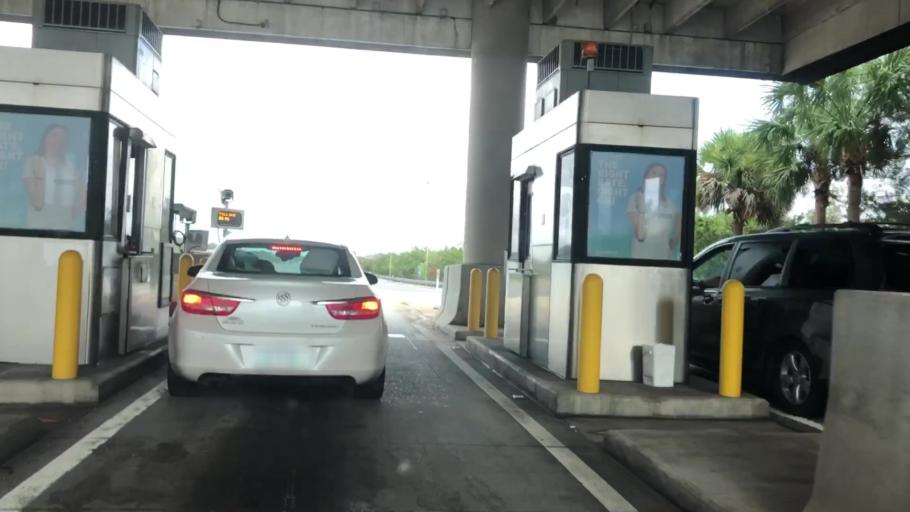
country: US
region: Florida
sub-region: Osceola County
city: Saint Cloud
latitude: 28.1817
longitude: -81.3029
